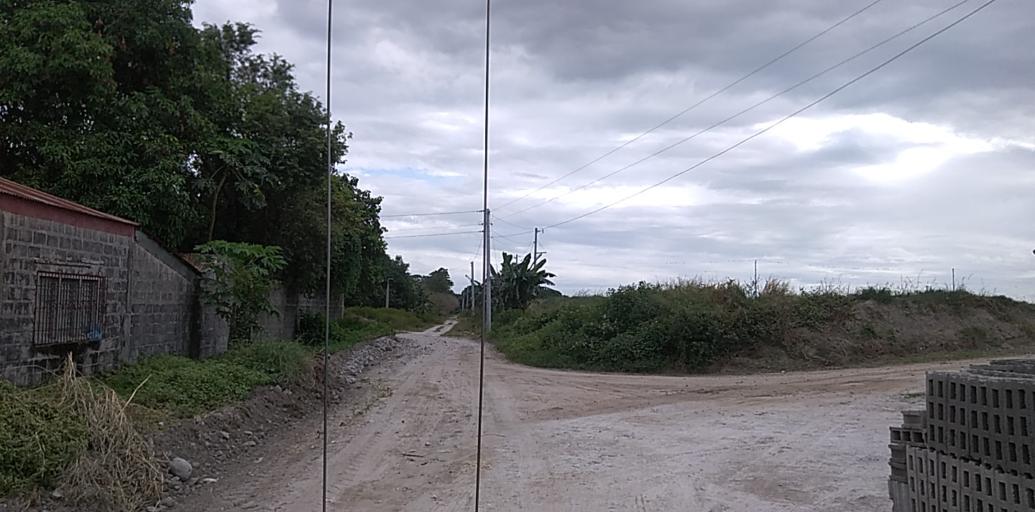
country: PH
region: Central Luzon
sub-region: Province of Pampanga
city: Pulung Santol
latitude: 15.0389
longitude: 120.5591
